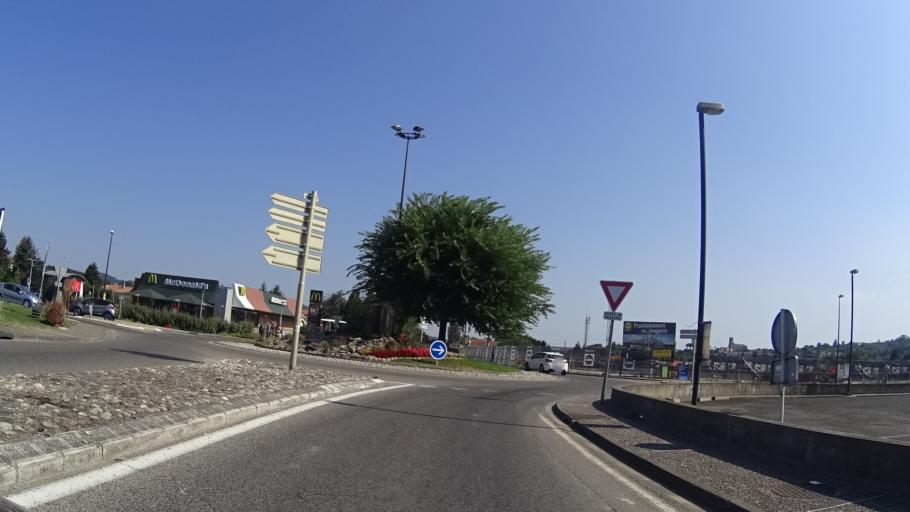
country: FR
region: Midi-Pyrenees
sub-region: Departement de l'Ariege
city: Lavelanet
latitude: 42.9627
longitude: 1.8644
